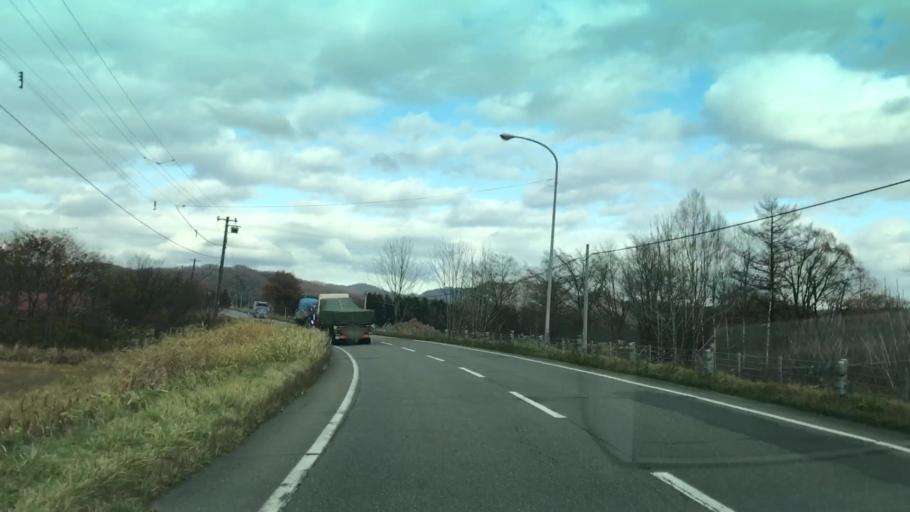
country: JP
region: Hokkaido
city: Shimo-furano
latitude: 42.8675
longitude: 142.4258
